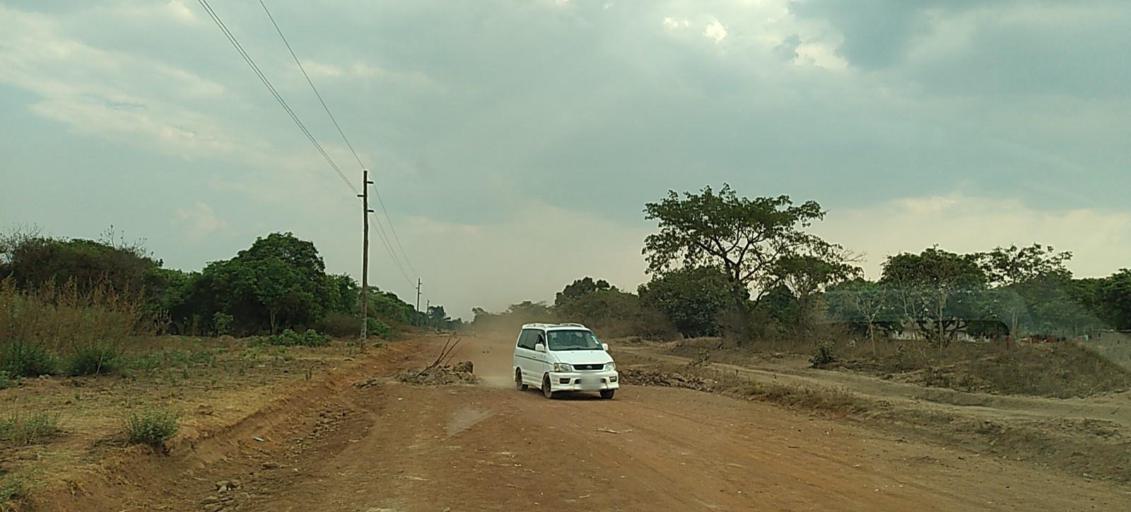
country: ZM
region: Copperbelt
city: Kalulushi
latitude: -12.8933
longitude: 27.9503
